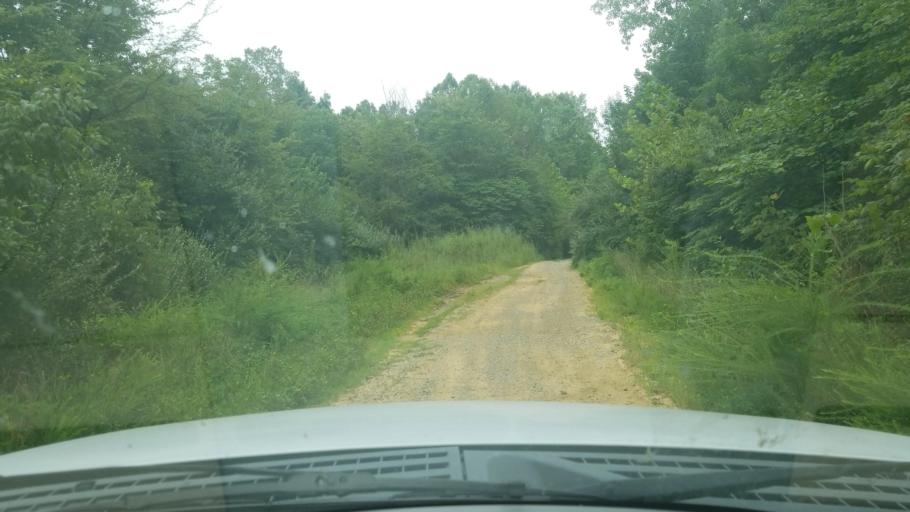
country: US
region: Illinois
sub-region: Saline County
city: Harrisburg
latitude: 37.8501
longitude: -88.5936
